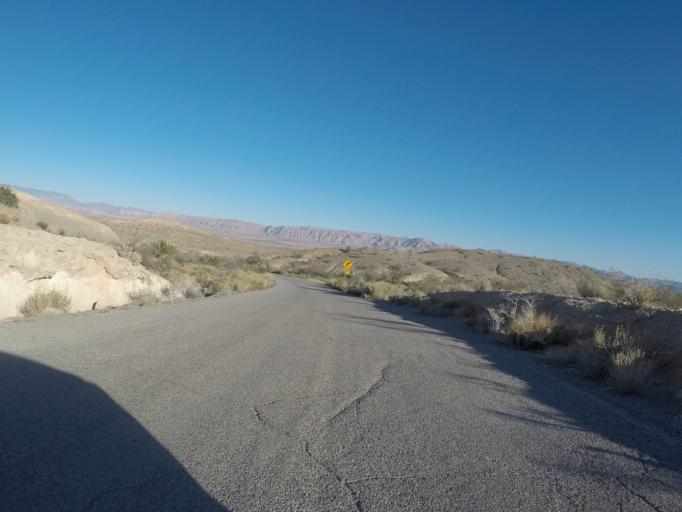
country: US
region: Nevada
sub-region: Clark County
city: Moapa Valley
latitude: 36.3894
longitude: -114.4210
